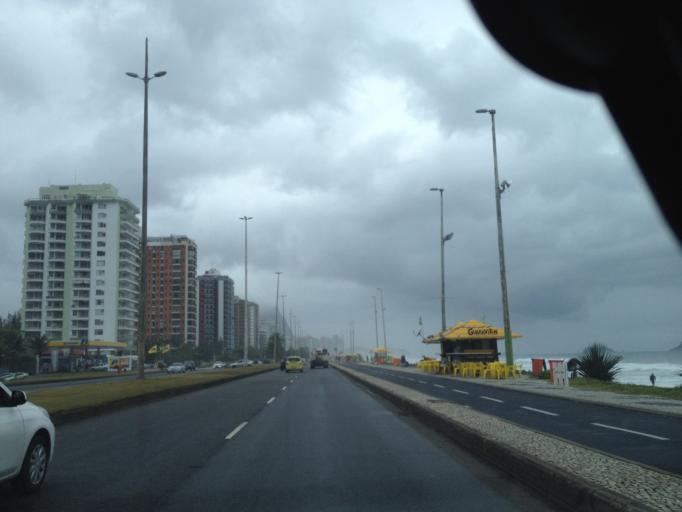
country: BR
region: Rio de Janeiro
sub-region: Rio De Janeiro
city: Rio de Janeiro
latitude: -23.0107
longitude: -43.3612
